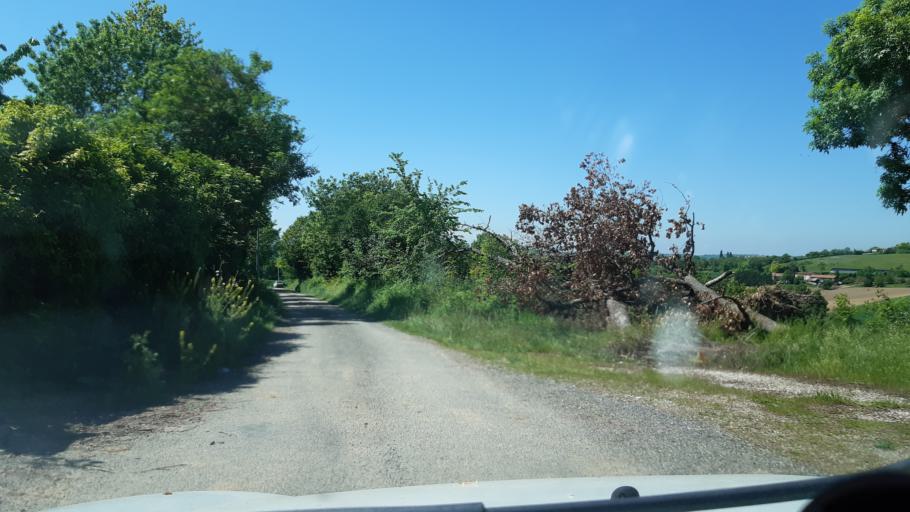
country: FR
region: Midi-Pyrenees
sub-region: Departement du Gers
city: Samatan
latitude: 43.5061
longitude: 1.0073
